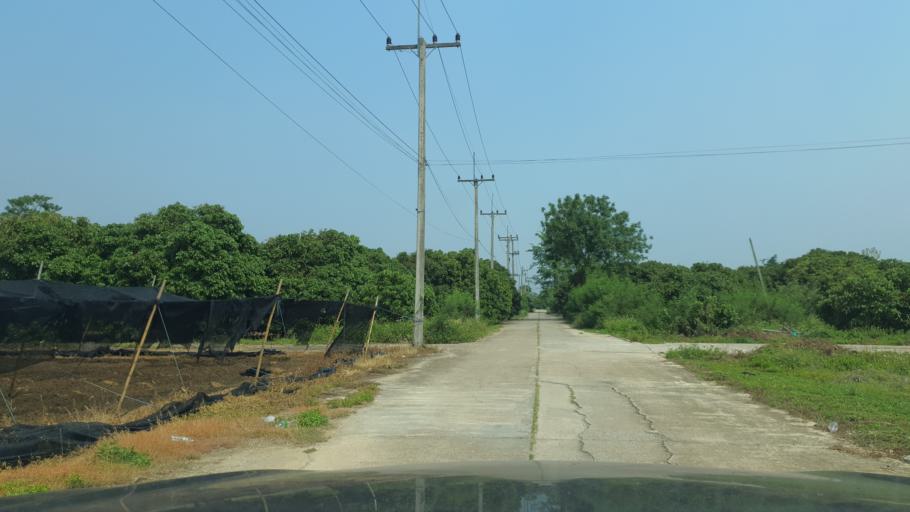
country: TH
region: Chiang Mai
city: Saraphi
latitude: 18.6699
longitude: 98.9898
